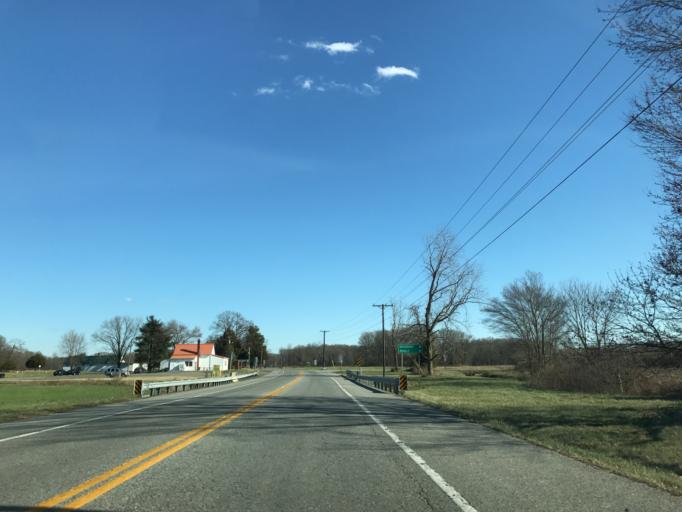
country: US
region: Maryland
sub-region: Caroline County
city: Greensboro
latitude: 39.0595
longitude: -75.8463
